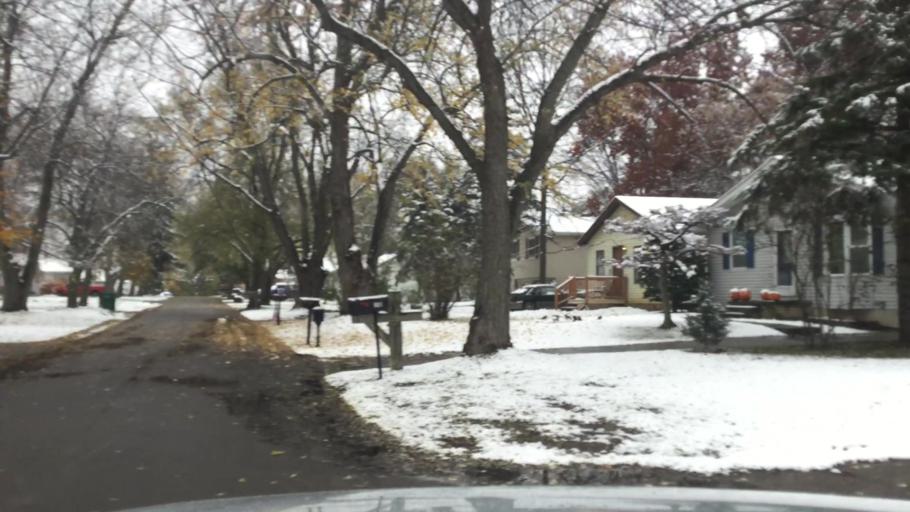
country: US
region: Michigan
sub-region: Oakland County
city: Oxford
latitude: 42.8104
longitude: -83.2951
